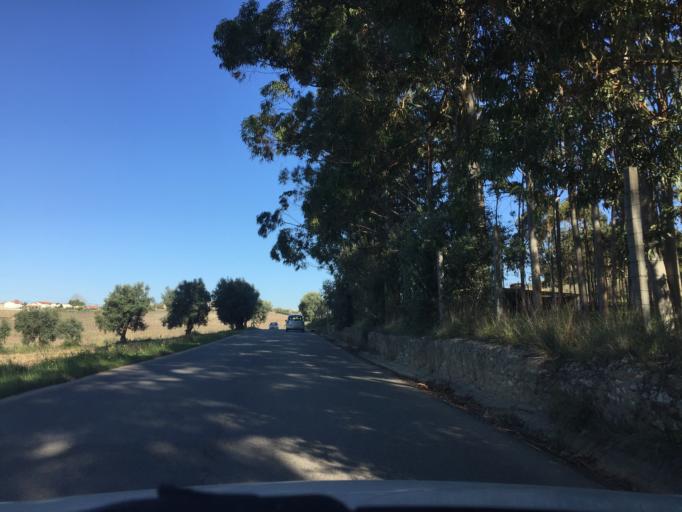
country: PT
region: Aveiro
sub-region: Anadia
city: Sangalhos
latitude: 40.4619
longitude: -8.4979
